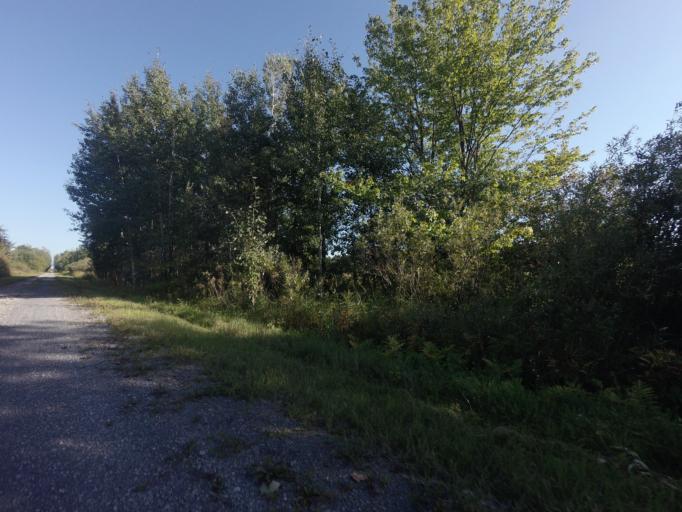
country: CA
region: Ontario
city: Hawkesbury
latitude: 45.5359
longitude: -74.5986
